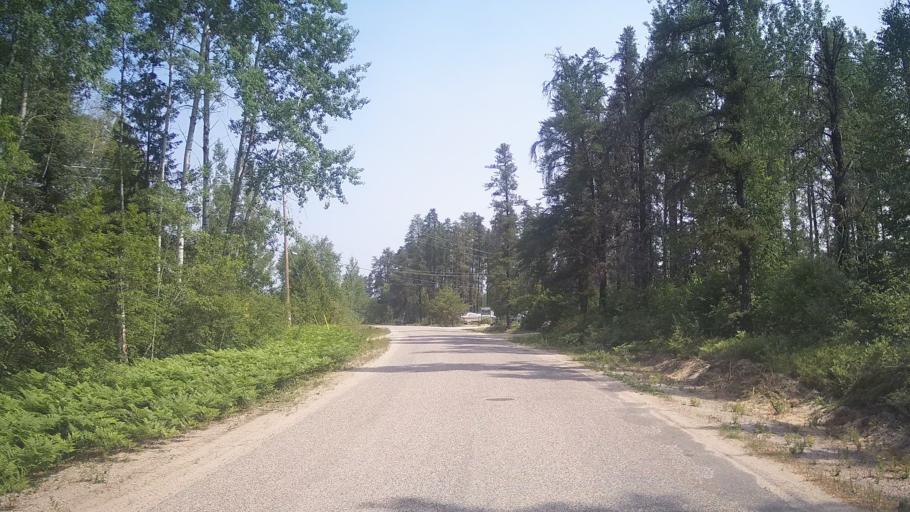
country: CA
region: Ontario
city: Timmins
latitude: 47.6817
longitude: -81.7142
